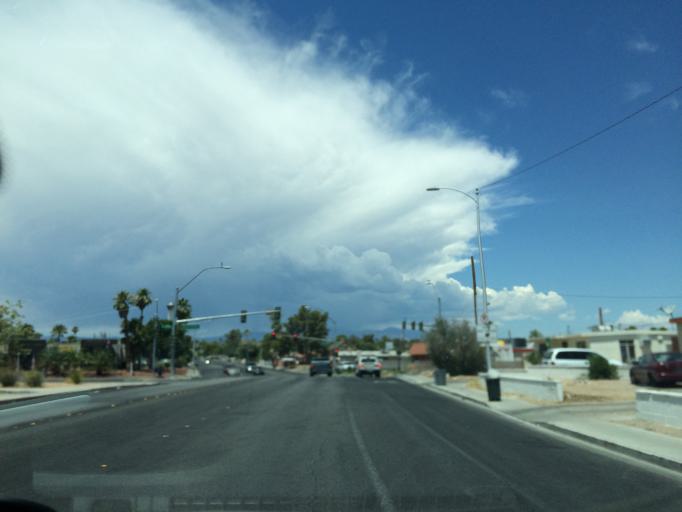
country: US
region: Nevada
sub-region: Clark County
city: Winchester
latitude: 36.1482
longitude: -115.1179
